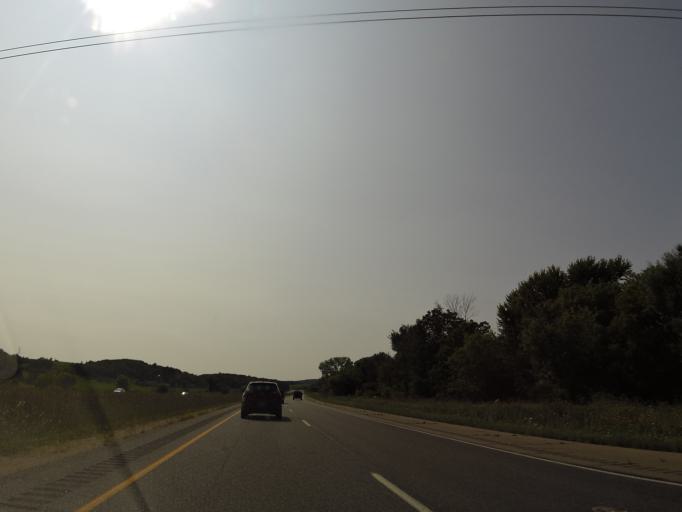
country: US
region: Wisconsin
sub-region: Monroe County
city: Tomah
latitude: 43.9474
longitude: -90.5521
